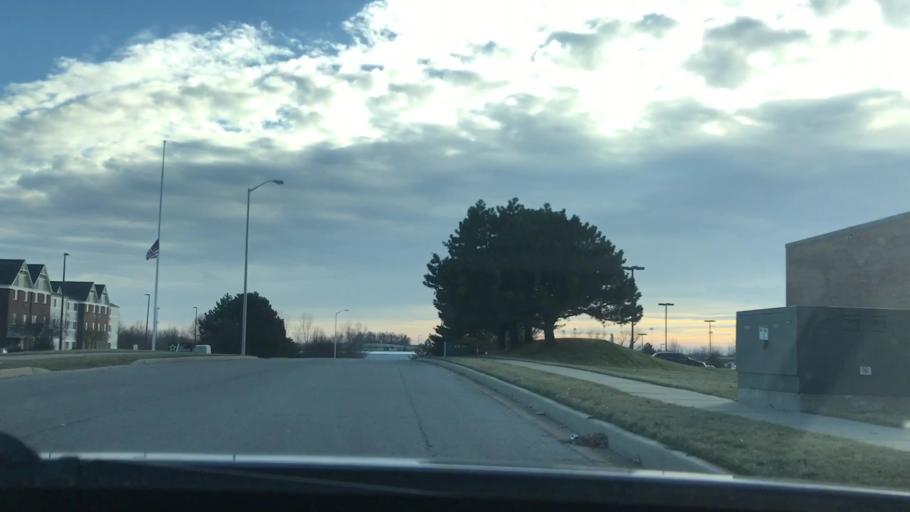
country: US
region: Missouri
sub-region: Platte County
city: Weatherby Lake
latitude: 39.2698
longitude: -94.6695
